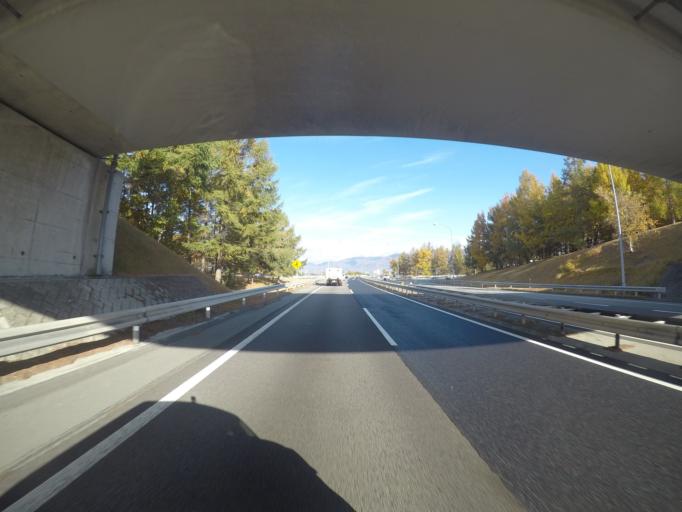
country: JP
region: Nagano
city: Komoro
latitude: 36.2870
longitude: 138.4836
